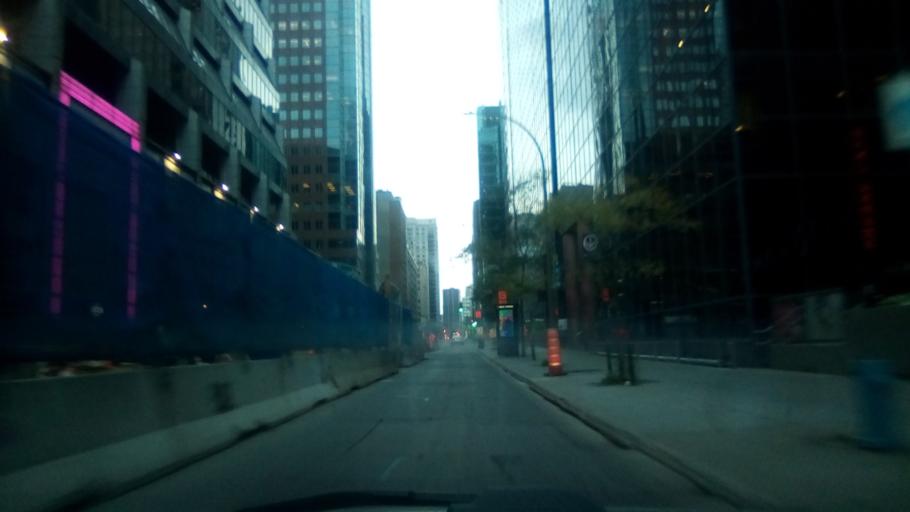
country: CA
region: Quebec
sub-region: Montreal
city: Montreal
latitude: 45.5034
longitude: -73.5719
